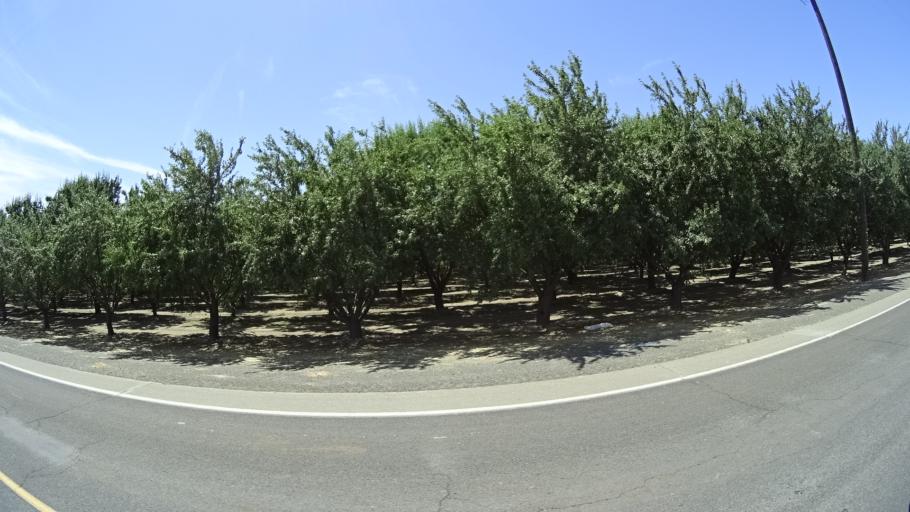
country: US
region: California
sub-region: Kings County
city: Armona
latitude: 36.3426
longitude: -119.7497
